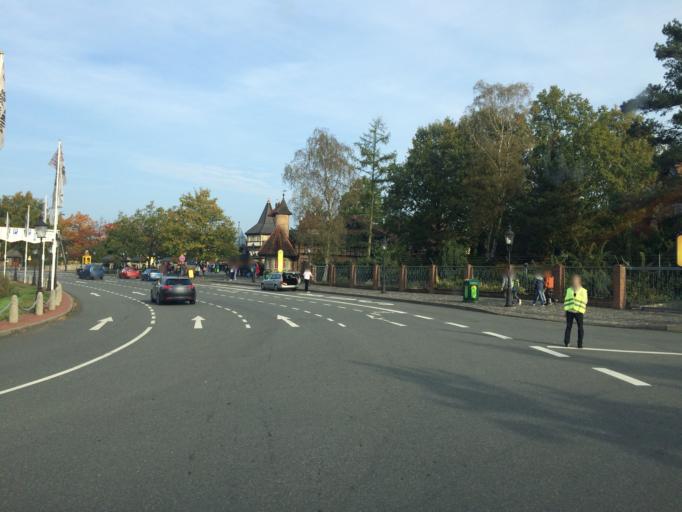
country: DE
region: Lower Saxony
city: Soltau
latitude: 53.0216
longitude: 9.8733
